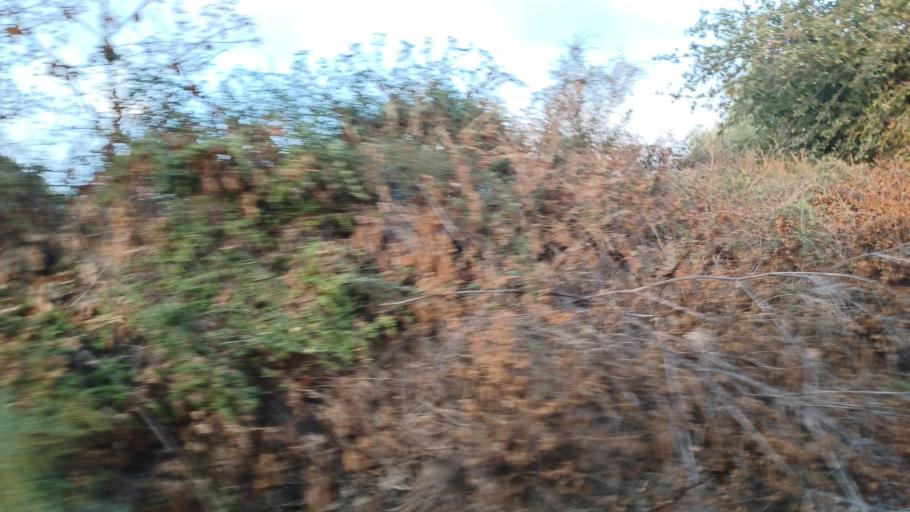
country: CY
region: Pafos
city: Mesogi
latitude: 34.8222
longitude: 32.5777
